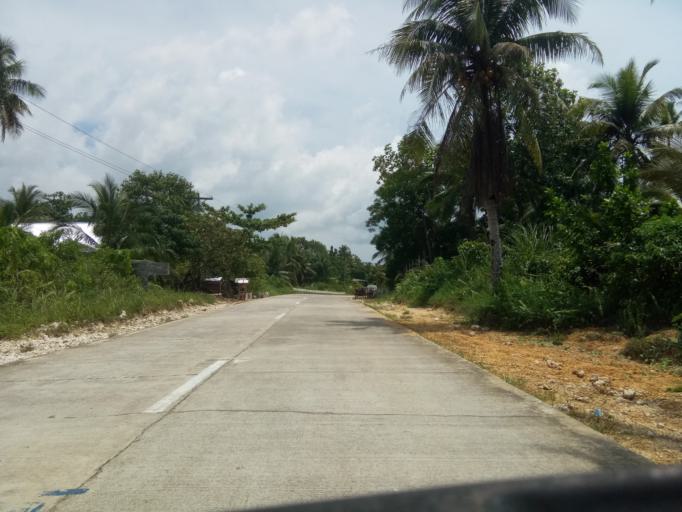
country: PH
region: Caraga
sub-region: Province of Surigao del Norte
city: San Isidro
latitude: 9.9280
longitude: 126.0999
